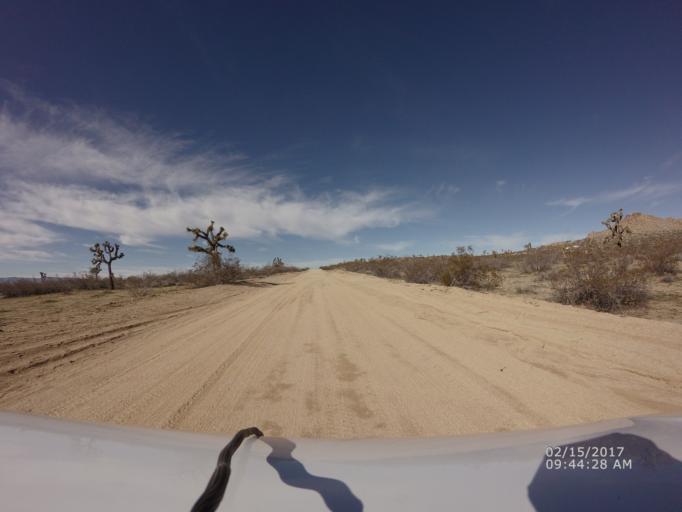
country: US
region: California
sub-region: Los Angeles County
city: Lake Los Angeles
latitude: 34.6238
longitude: -117.8929
